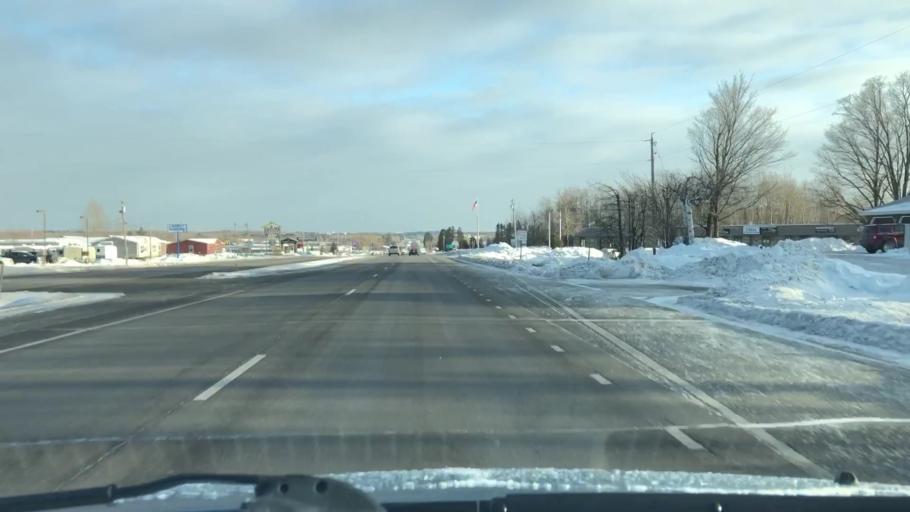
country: US
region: Minnesota
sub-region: Saint Louis County
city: Hermantown
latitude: 46.8253
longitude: -92.1921
